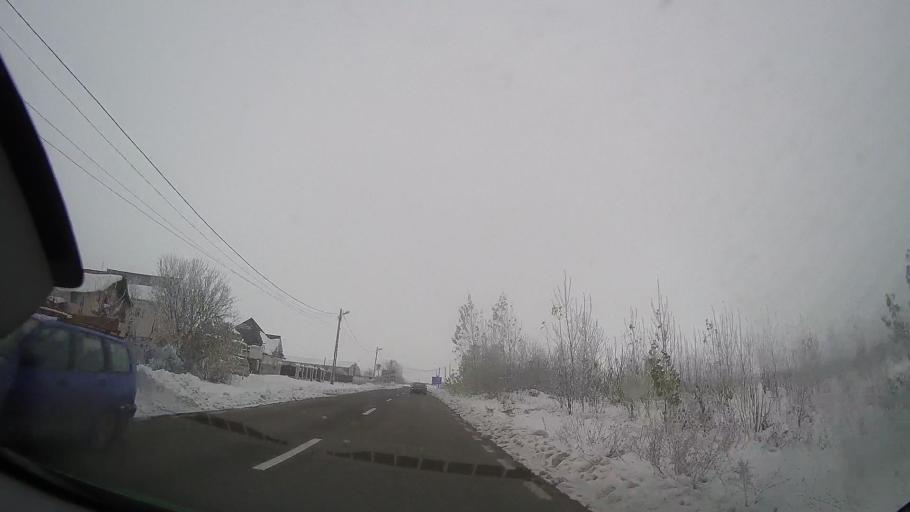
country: RO
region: Neamt
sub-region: Comuna Horia
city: Cotu Vames
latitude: 46.9370
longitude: 26.9468
